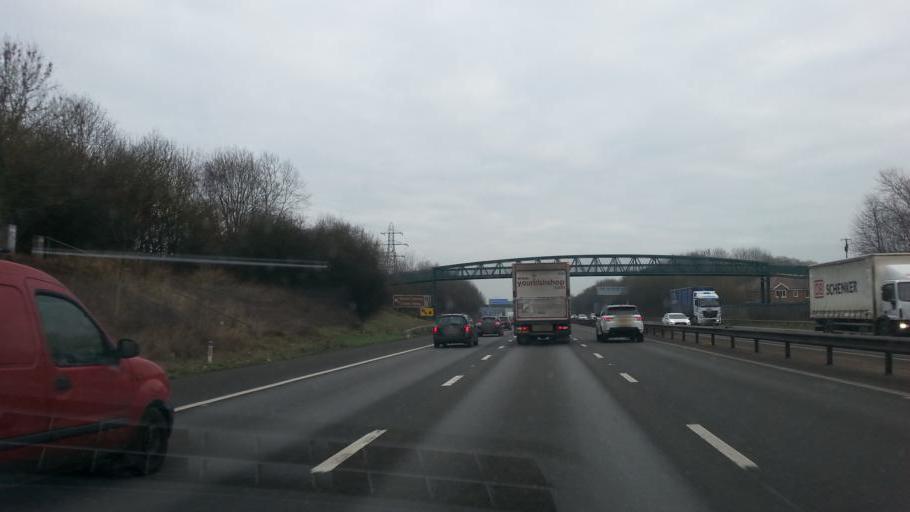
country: GB
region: England
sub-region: Warwickshire
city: Exhall
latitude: 52.4430
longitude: -1.4485
